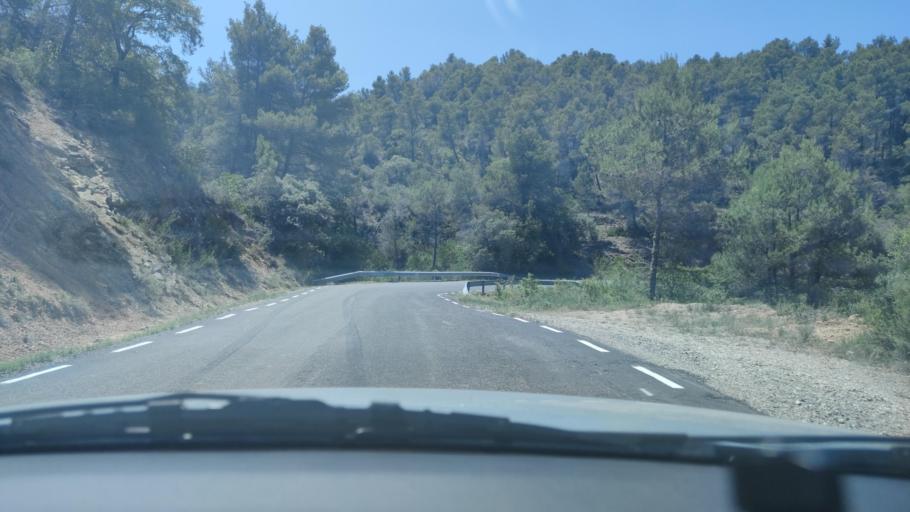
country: ES
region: Catalonia
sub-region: Provincia de Tarragona
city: Ulldemolins
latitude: 41.3469
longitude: 0.8833
